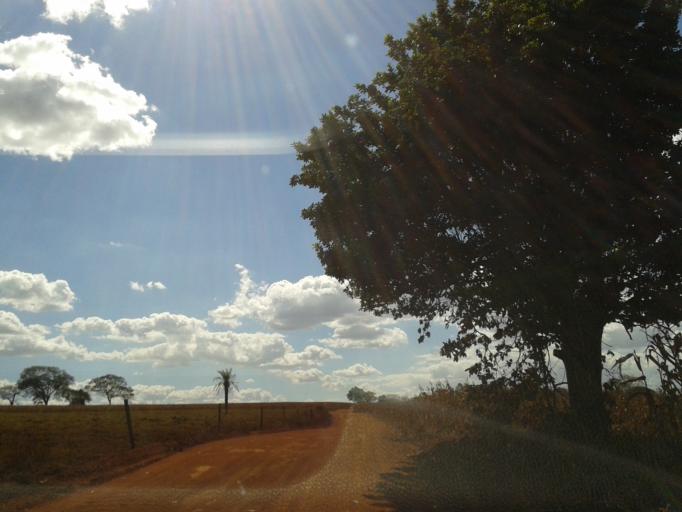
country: BR
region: Minas Gerais
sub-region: Capinopolis
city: Capinopolis
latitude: -18.6078
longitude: -49.4953
